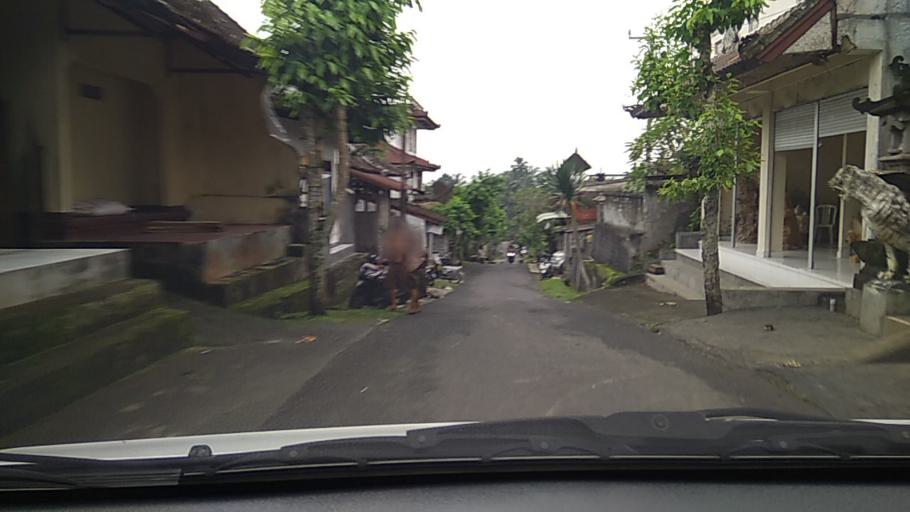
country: ID
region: Bali
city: Banjar Dujung Kaja
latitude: -8.4168
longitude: 115.2825
